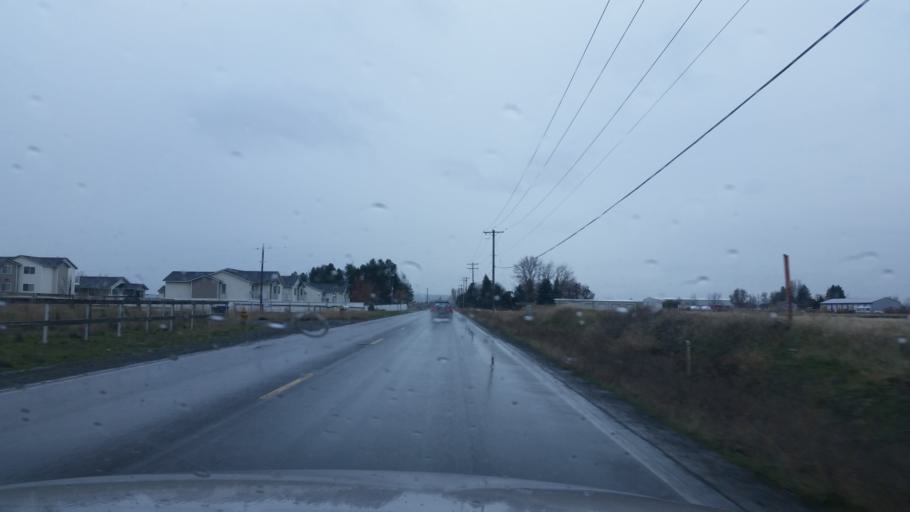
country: US
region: Washington
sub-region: Spokane County
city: Airway Heights
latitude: 47.6402
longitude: -117.5609
